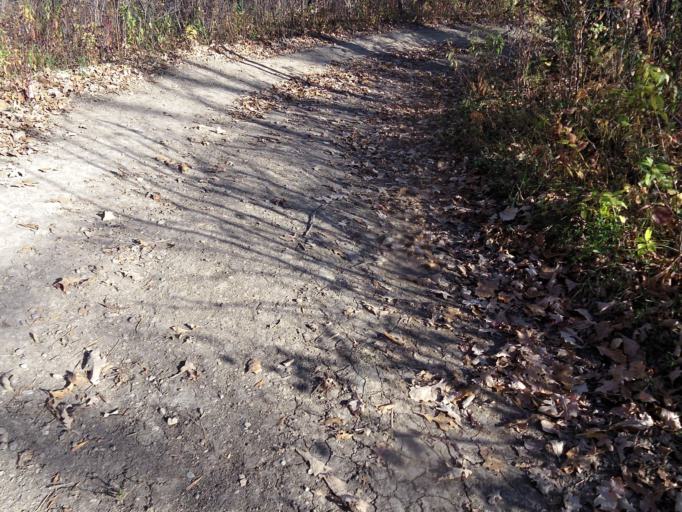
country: CA
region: Manitoba
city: Morden
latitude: 48.9440
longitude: -98.0670
